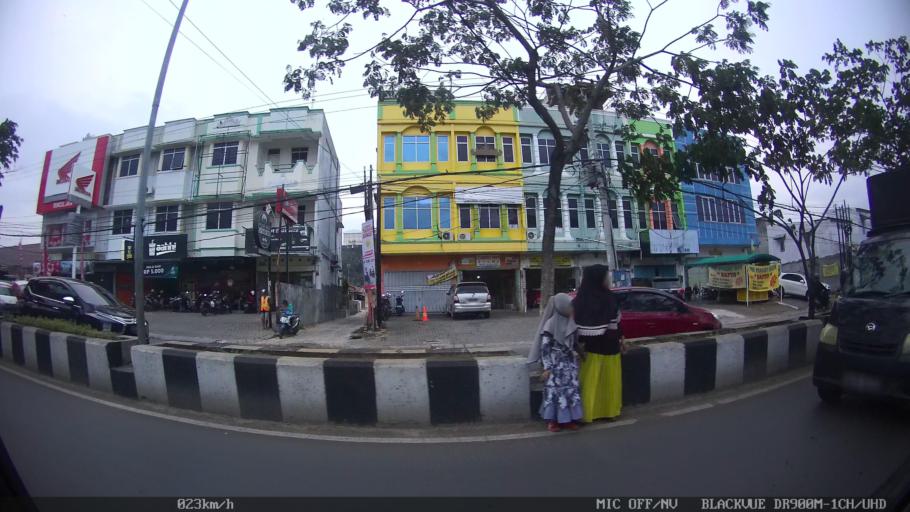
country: ID
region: Lampung
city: Bandarlampung
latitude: -5.4117
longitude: 105.2672
